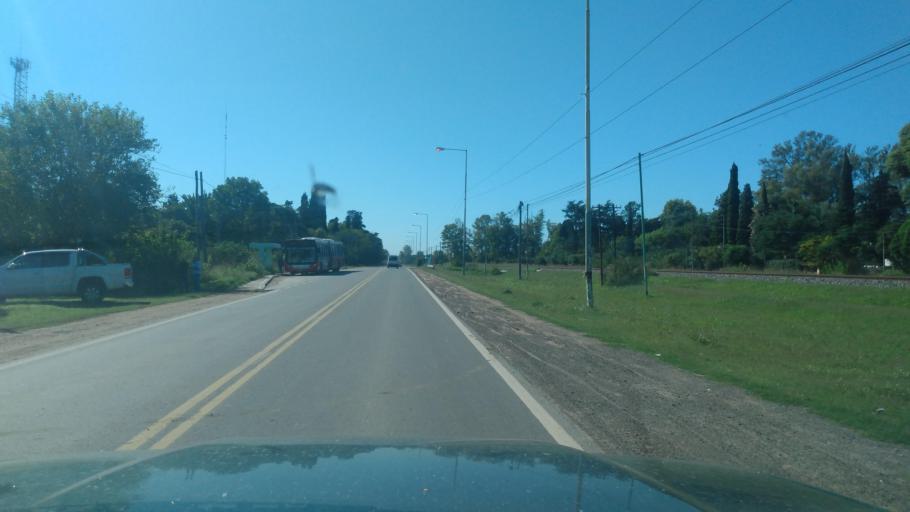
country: AR
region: Buenos Aires
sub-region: Partido de General Rodriguez
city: General Rodriguez
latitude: -34.6040
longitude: -58.9725
